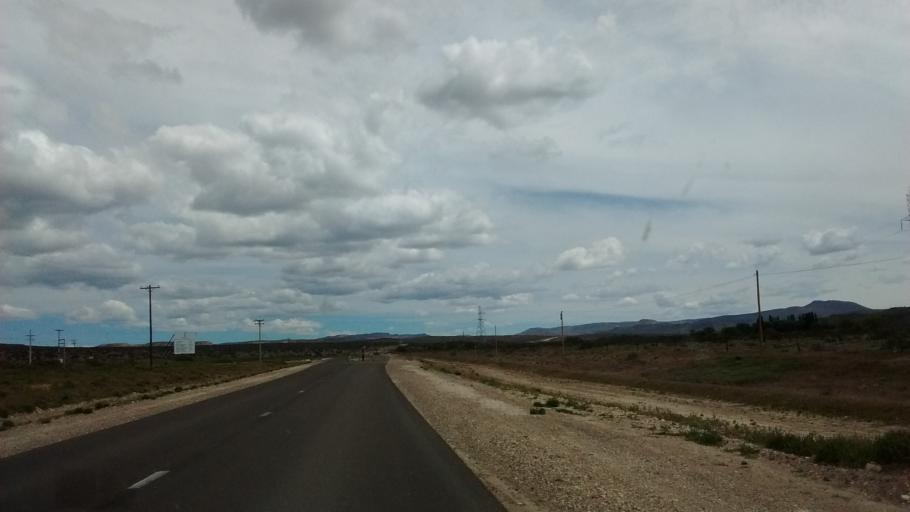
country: AR
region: Neuquen
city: Piedra del Aguila
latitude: -40.0711
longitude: -70.1203
